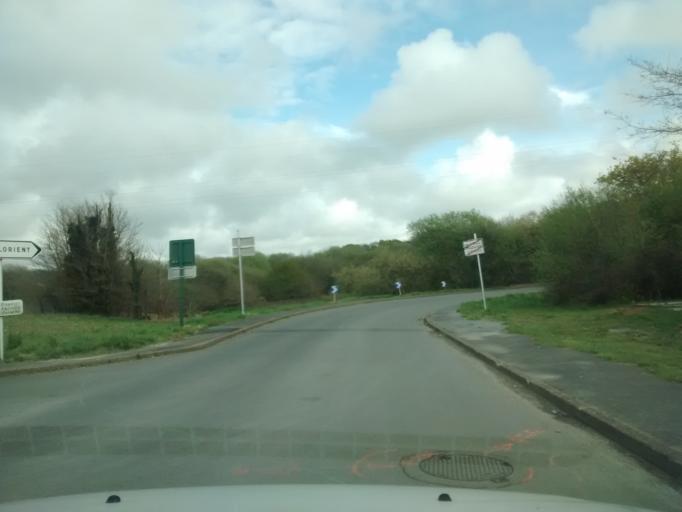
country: FR
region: Brittany
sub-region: Departement du Morbihan
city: Gestel
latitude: 47.7881
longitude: -3.4800
